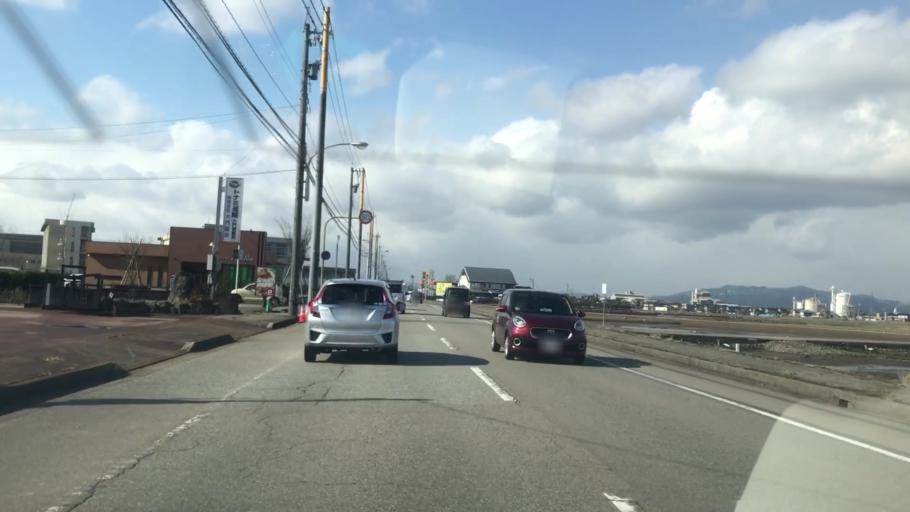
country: JP
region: Toyama
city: Nishishinminato
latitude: 36.7245
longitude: 137.0669
